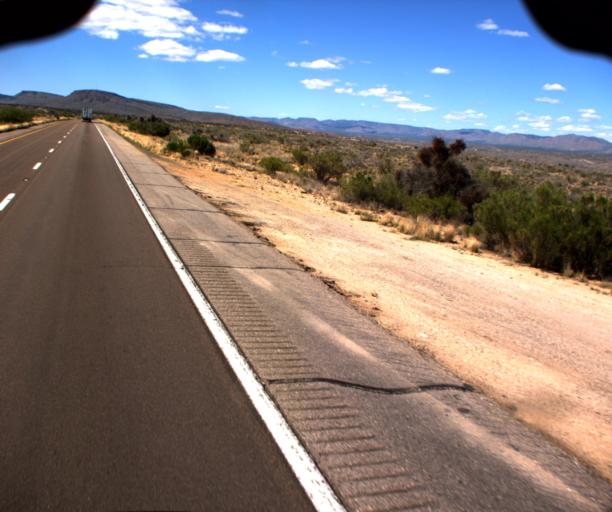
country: US
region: Arizona
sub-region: Mohave County
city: Kingman
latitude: 35.1108
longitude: -113.6660
